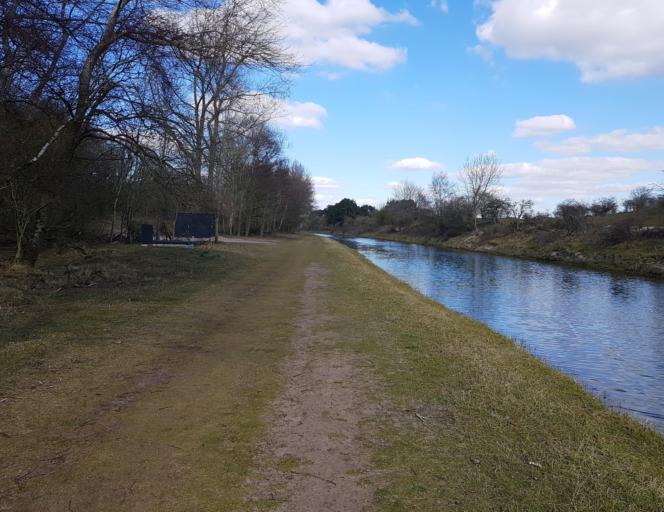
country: NL
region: South Holland
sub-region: Gemeente Hillegom
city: Hillegom
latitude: 52.3088
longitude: 4.5344
